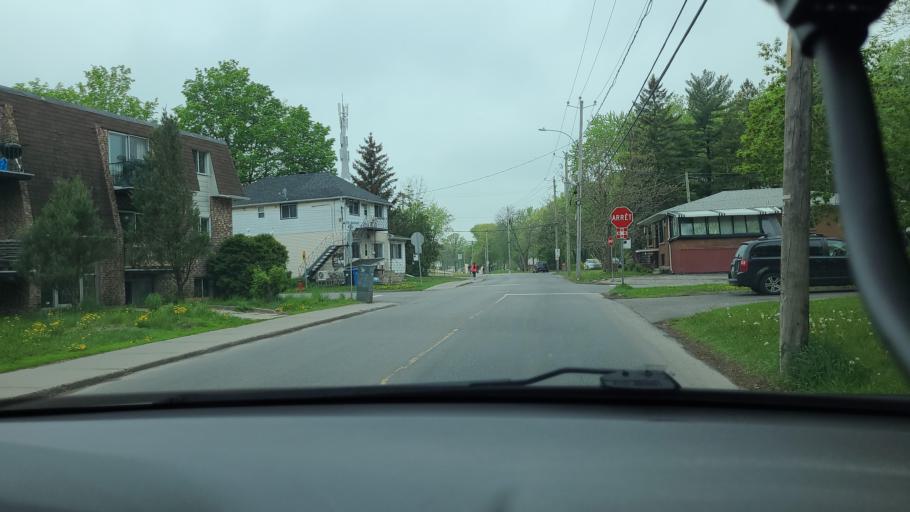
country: CA
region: Quebec
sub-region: Monteregie
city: L'Ile-Perrot
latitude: 45.3932
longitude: -73.9497
